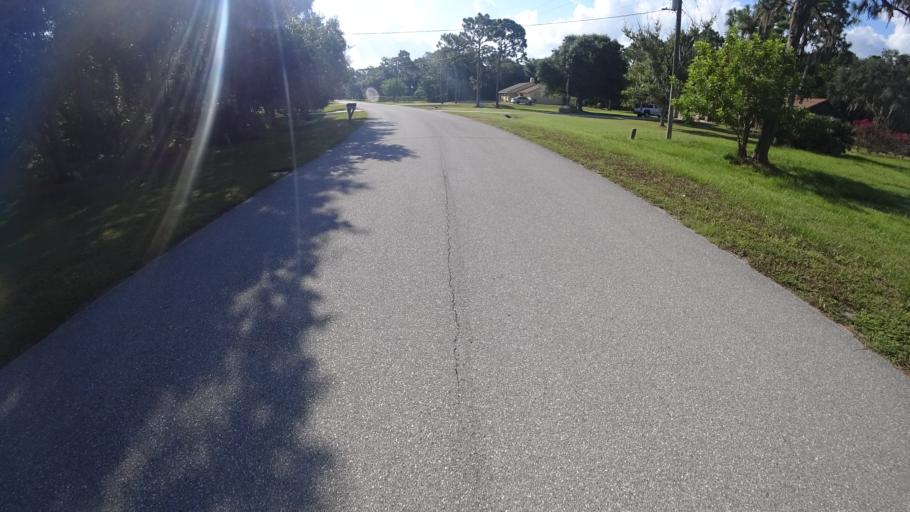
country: US
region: Florida
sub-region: Sarasota County
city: The Meadows
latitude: 27.4243
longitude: -82.4517
